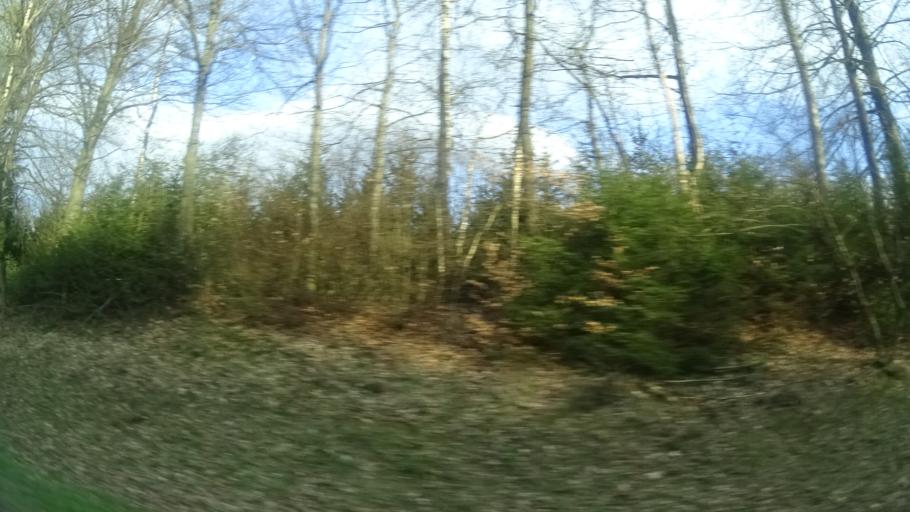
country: DE
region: Bavaria
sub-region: Upper Franconia
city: Leupoldsgrun
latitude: 50.2953
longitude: 11.8187
